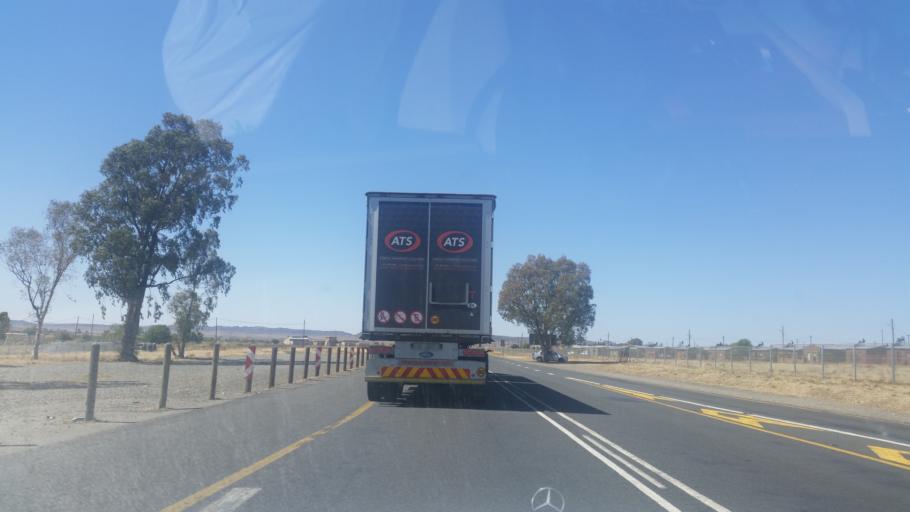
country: ZA
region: Northern Cape
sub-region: Pixley ka Seme District Municipality
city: Colesberg
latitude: -30.7079
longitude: 25.1092
